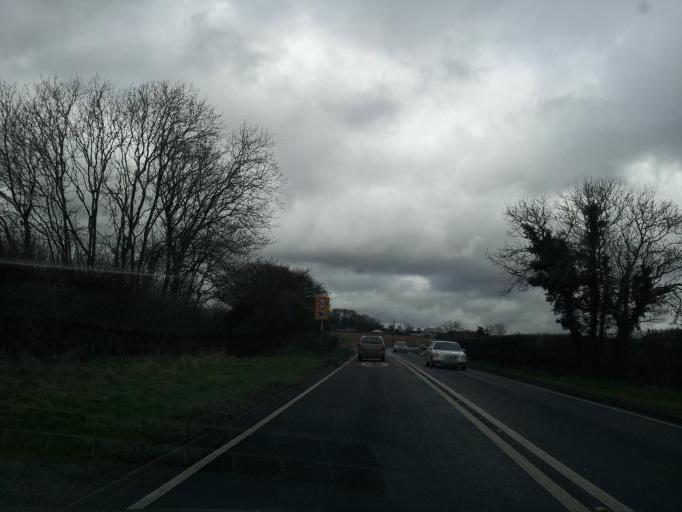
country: GB
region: England
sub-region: Somerset
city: Ilchester
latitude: 51.0245
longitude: -2.6082
